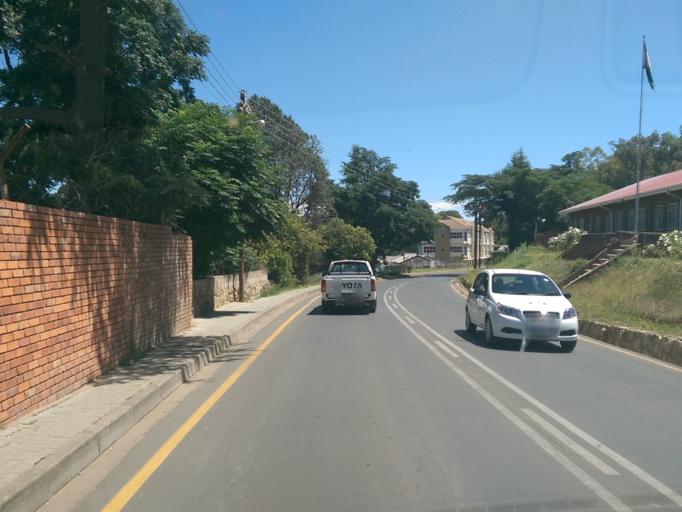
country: LS
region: Maseru
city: Maseru
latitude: -29.3117
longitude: 27.4793
